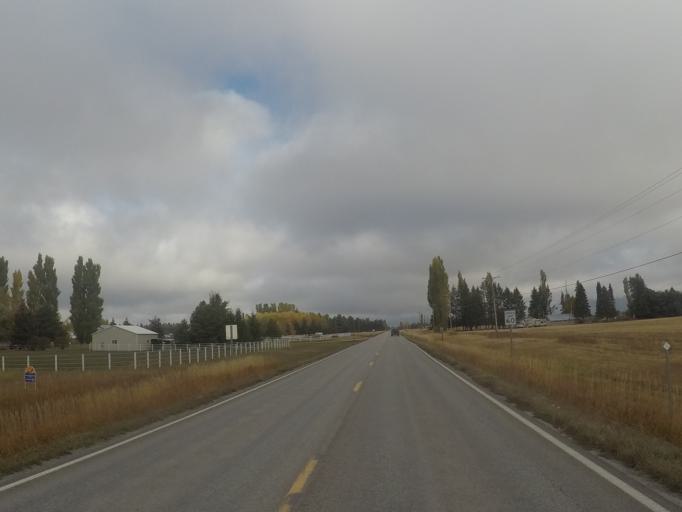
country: US
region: Montana
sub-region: Flathead County
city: Columbia Falls
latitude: 48.3250
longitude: -114.1594
